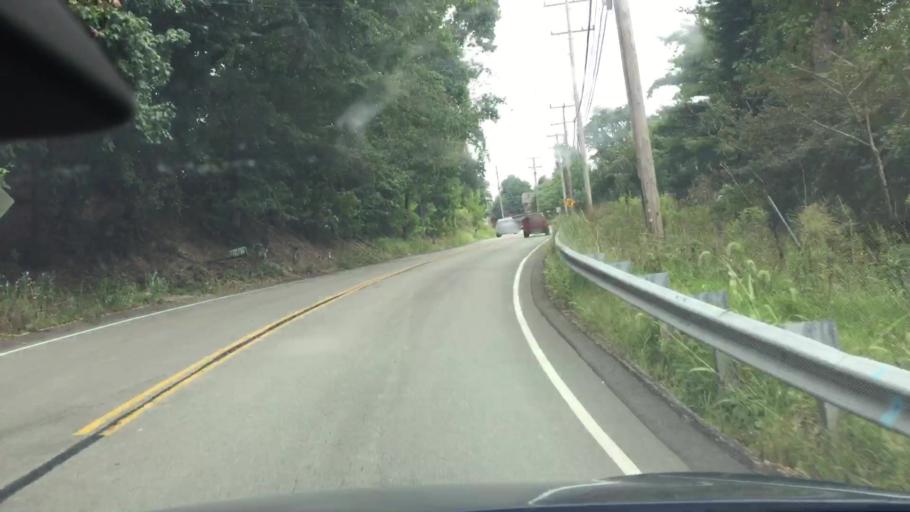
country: US
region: Pennsylvania
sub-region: Allegheny County
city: Monroeville
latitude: 40.4323
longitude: -79.7770
